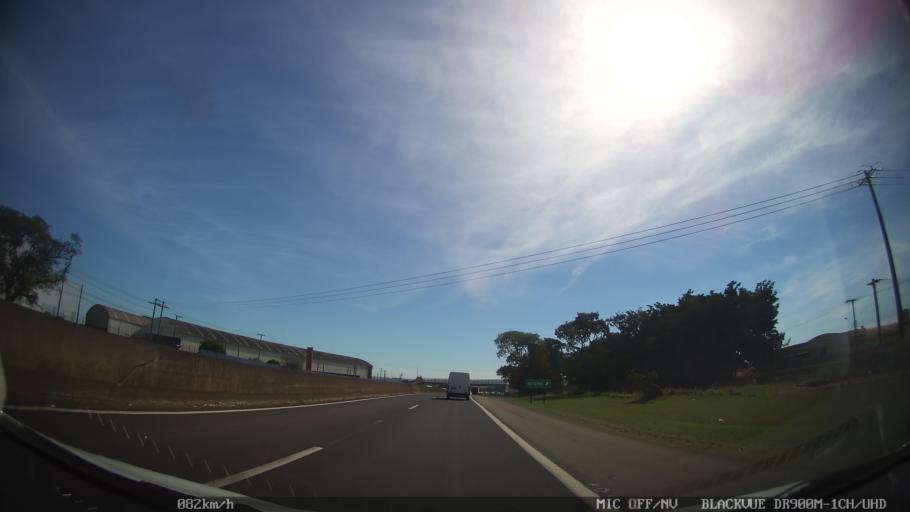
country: BR
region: Sao Paulo
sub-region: Porto Ferreira
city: Porto Ferreira
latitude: -21.8555
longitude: -47.4943
